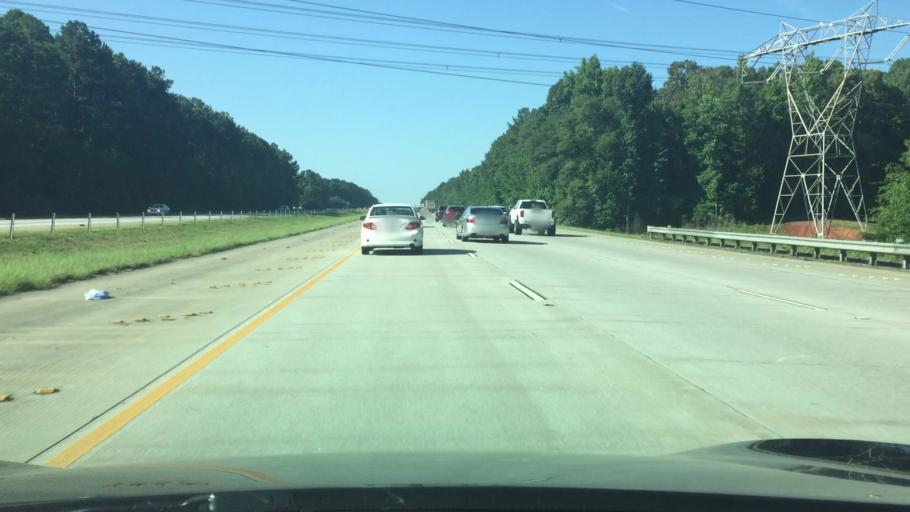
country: US
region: Georgia
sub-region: Coweta County
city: East Newnan
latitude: 33.2919
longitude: -84.7957
